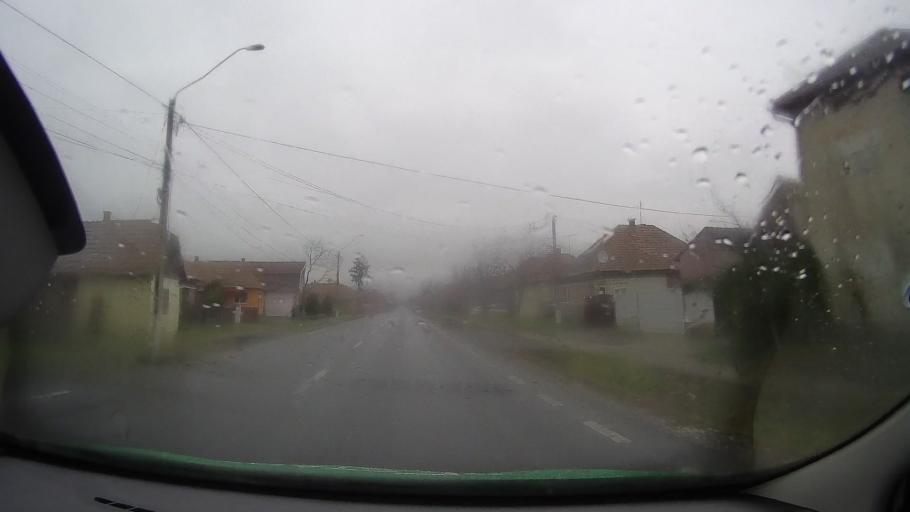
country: RO
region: Mures
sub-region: Comuna Suseni
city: Suseni
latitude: 46.8083
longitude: 24.7279
